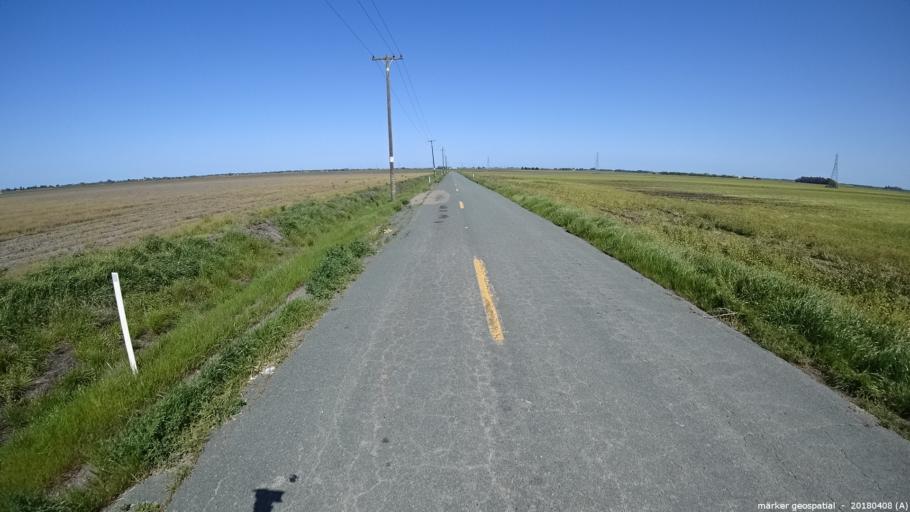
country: US
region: California
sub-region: Sacramento County
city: Walnut Grove
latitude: 38.3050
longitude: -121.5564
